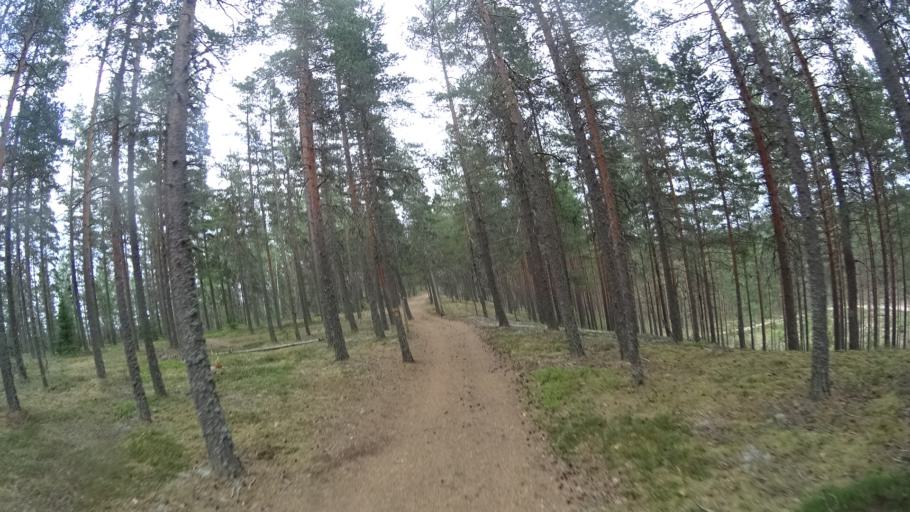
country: FI
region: Satakunta
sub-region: Pohjois-Satakunta
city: Jaemijaervi
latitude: 61.7737
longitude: 22.7298
